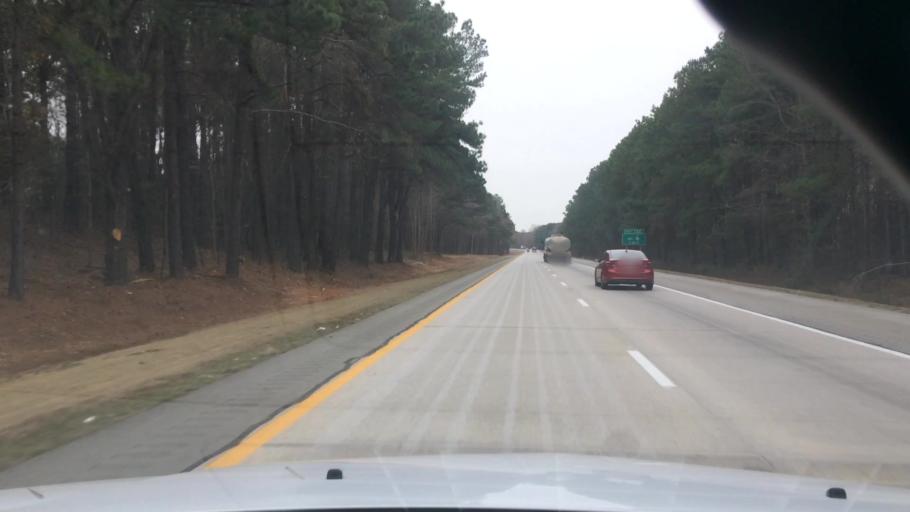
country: US
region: North Carolina
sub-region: Nash County
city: Nashville
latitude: 35.8878
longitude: -77.9399
